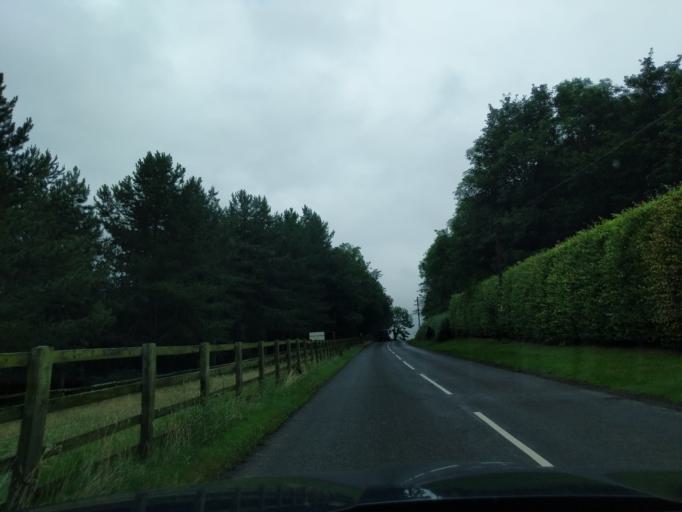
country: GB
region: England
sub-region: Northumberland
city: Ford
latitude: 55.6510
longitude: -2.1156
